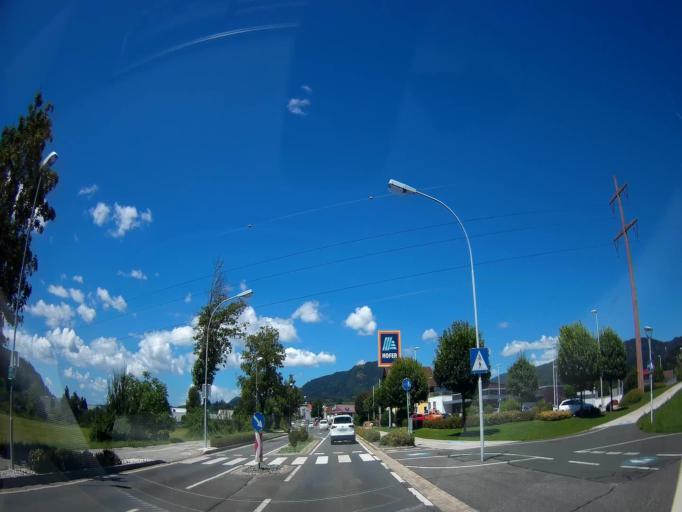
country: AT
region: Carinthia
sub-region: Politischer Bezirk Sankt Veit an der Glan
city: Sankt Veit an der Glan
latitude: 46.7661
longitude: 14.3761
